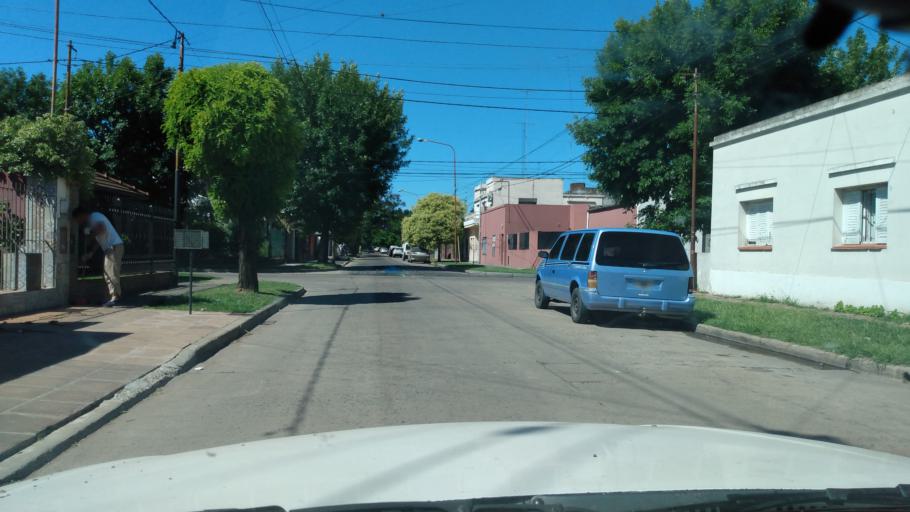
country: AR
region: Buenos Aires
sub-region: Partido de Lujan
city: Lujan
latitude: -34.5627
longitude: -59.1071
